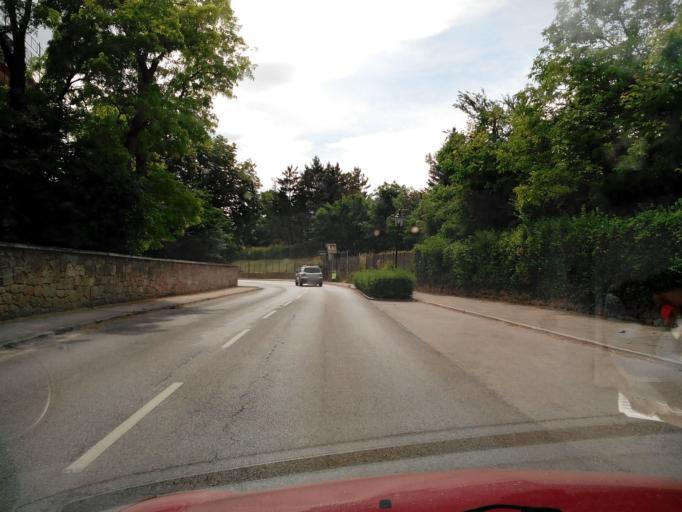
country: AT
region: Lower Austria
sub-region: Politischer Bezirk Wiener Neustadt
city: Weikersdorf am Steinfelde
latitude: 47.8346
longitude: 16.1704
